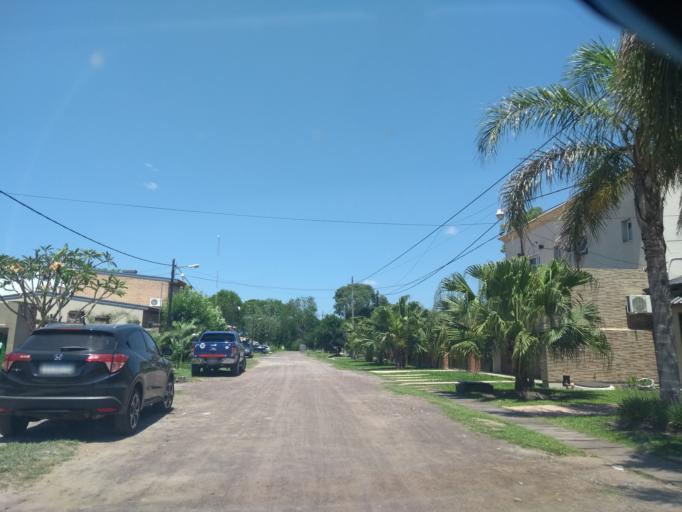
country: AR
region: Chaco
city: Resistencia
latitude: -27.4250
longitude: -58.9532
